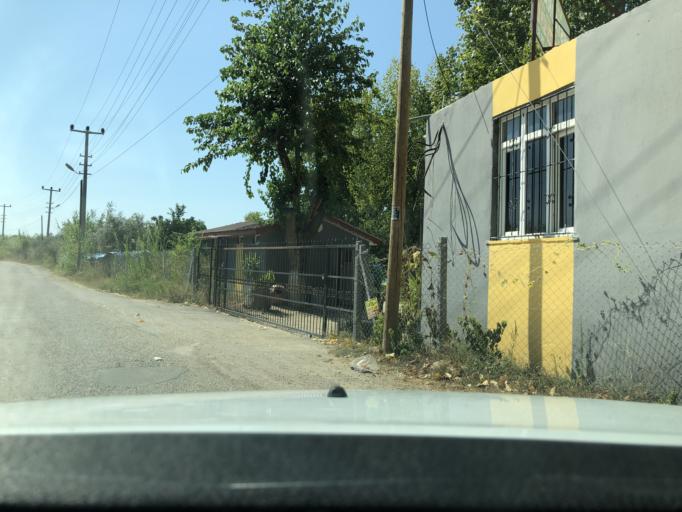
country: TR
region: Antalya
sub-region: Manavgat
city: Manavgat
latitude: 36.8076
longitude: 31.4641
